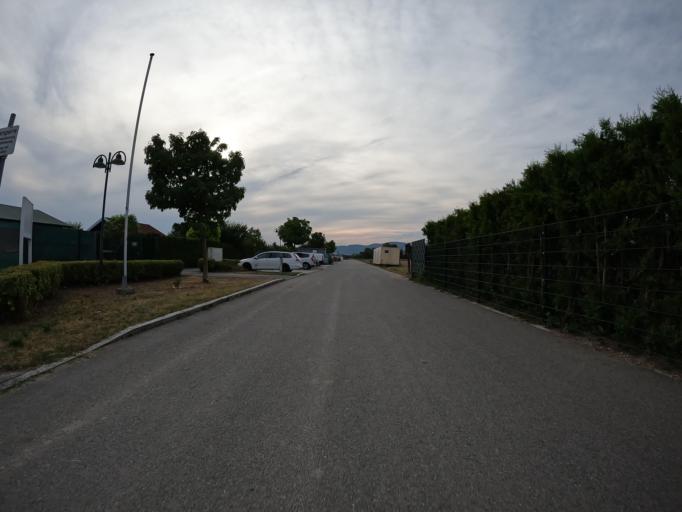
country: AT
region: Lower Austria
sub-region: Politischer Bezirk Baden
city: Trumau
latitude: 47.9986
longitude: 16.3370
